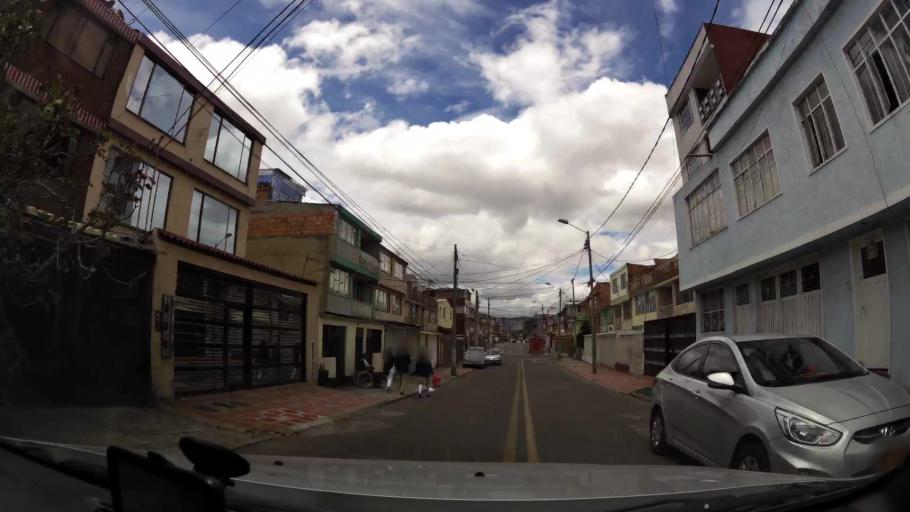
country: CO
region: Bogota D.C.
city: Bogota
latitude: 4.6058
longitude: -74.1064
